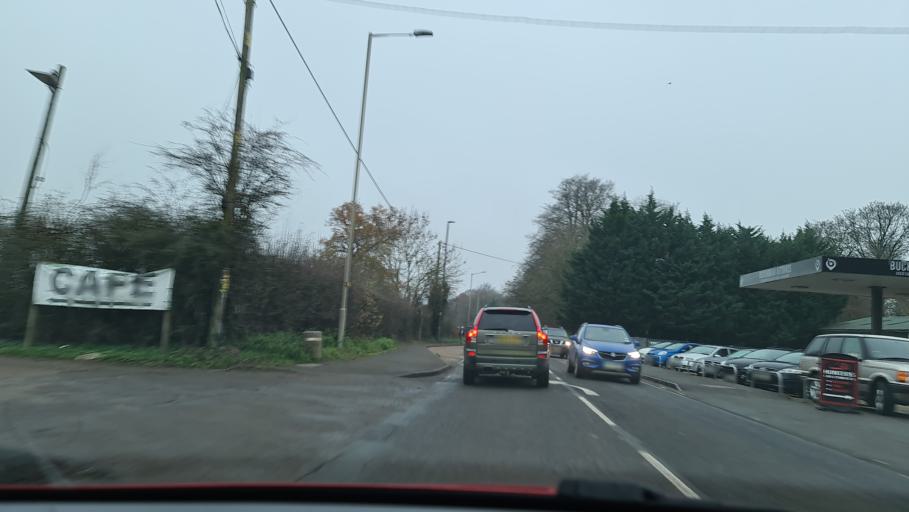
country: GB
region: England
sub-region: Buckinghamshire
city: Stokenchurch
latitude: 51.6491
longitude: -0.8584
